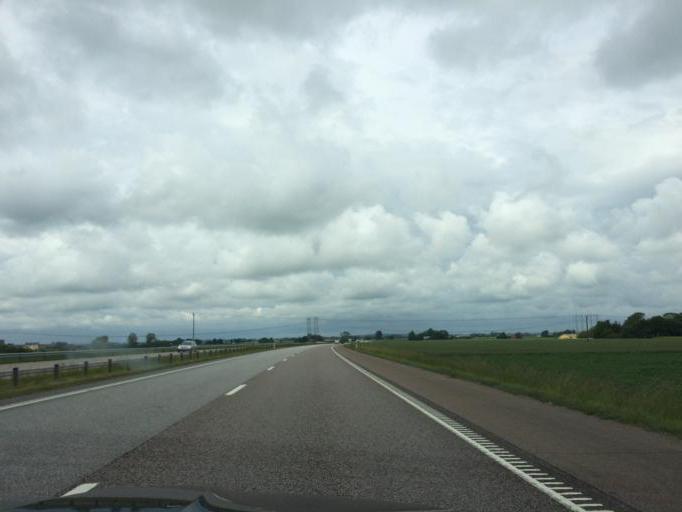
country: SE
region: Skane
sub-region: Angelholms Kommun
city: Strovelstorp
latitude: 56.1185
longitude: 12.8164
